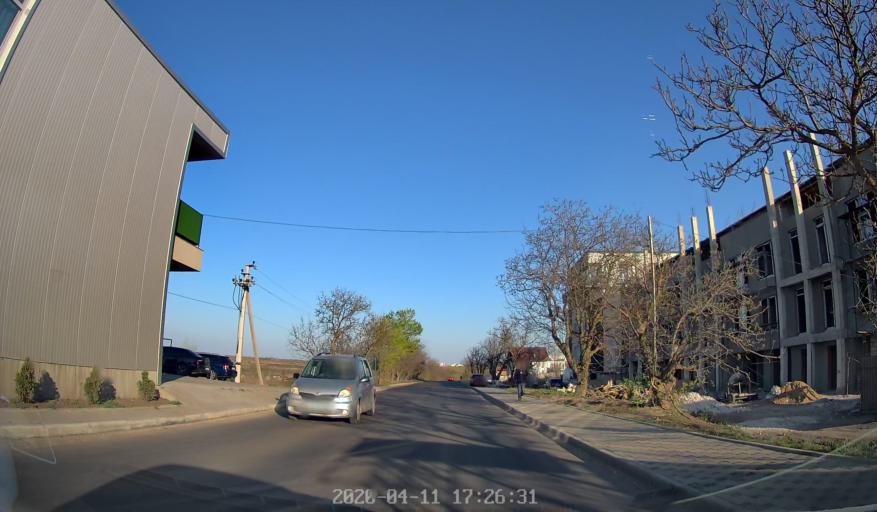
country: MD
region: Chisinau
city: Vatra
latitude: 47.0129
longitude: 28.7560
